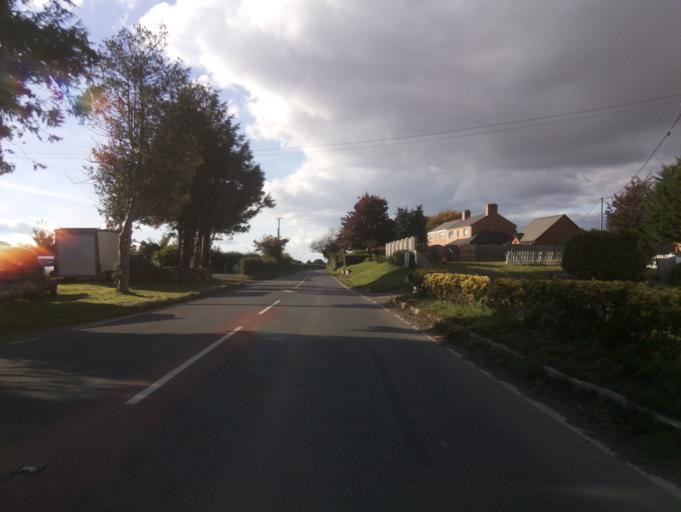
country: GB
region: England
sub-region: Herefordshire
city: Bridge Sollers
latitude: 52.0775
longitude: -2.8482
